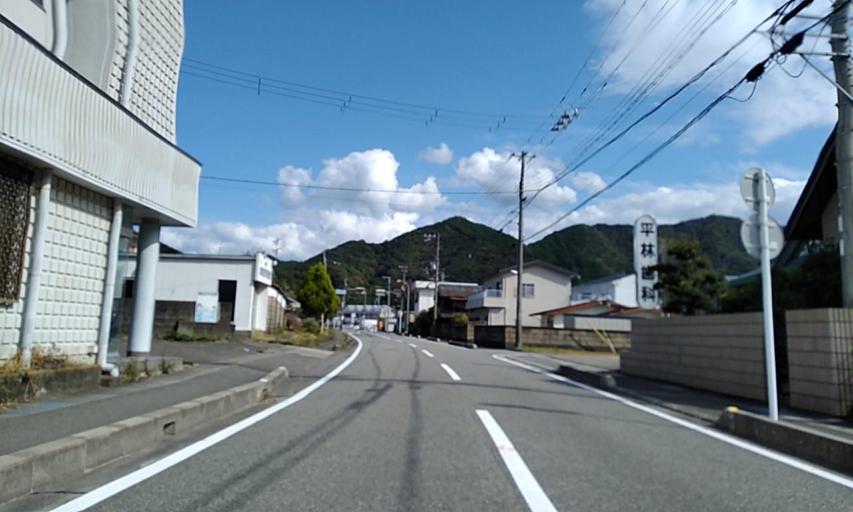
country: JP
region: Wakayama
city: Gobo
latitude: 33.9598
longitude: 135.1201
